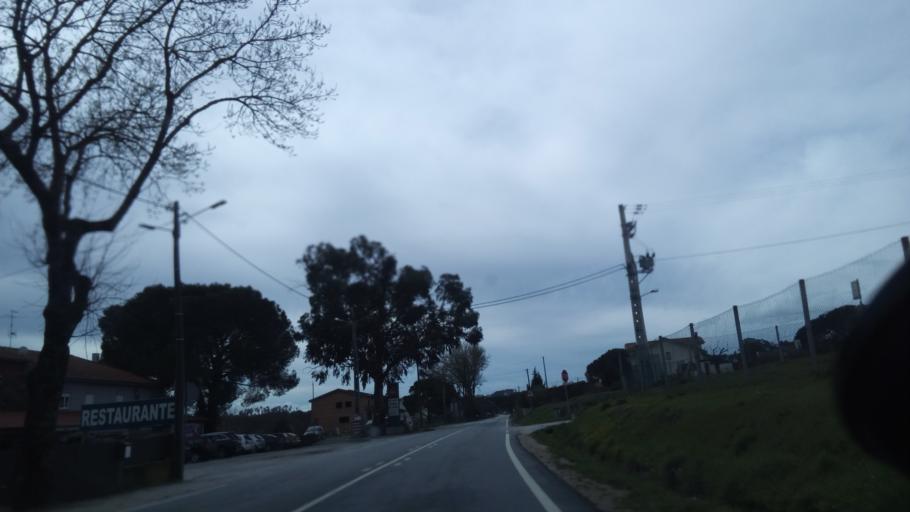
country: PT
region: Guarda
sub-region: Seia
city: Seia
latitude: 40.4600
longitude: -7.6910
